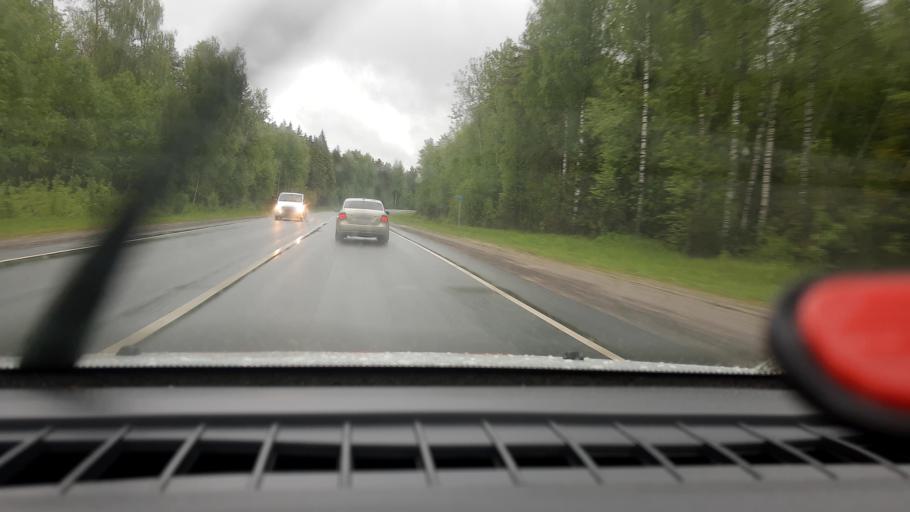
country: RU
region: Nizjnij Novgorod
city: Linda
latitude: 56.6377
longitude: 44.1051
